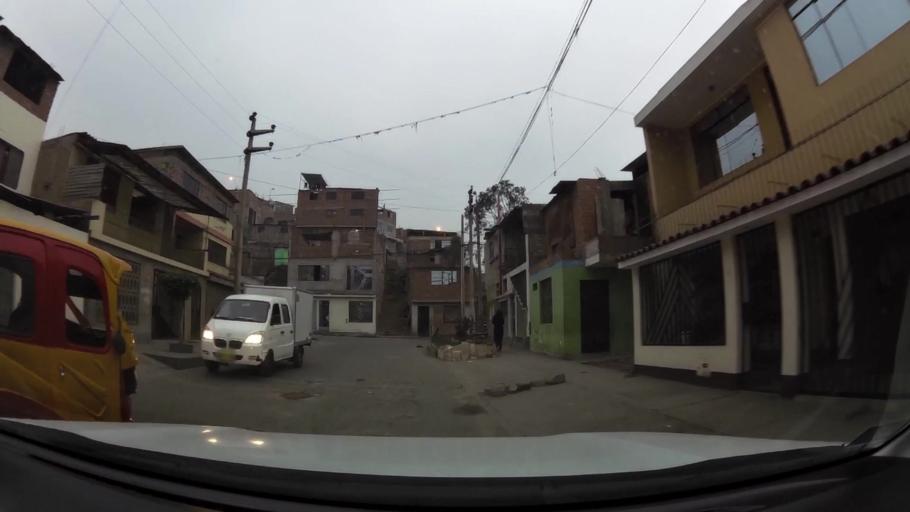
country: PE
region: Lima
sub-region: Lima
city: Surco
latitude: -12.1449
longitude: -76.9773
